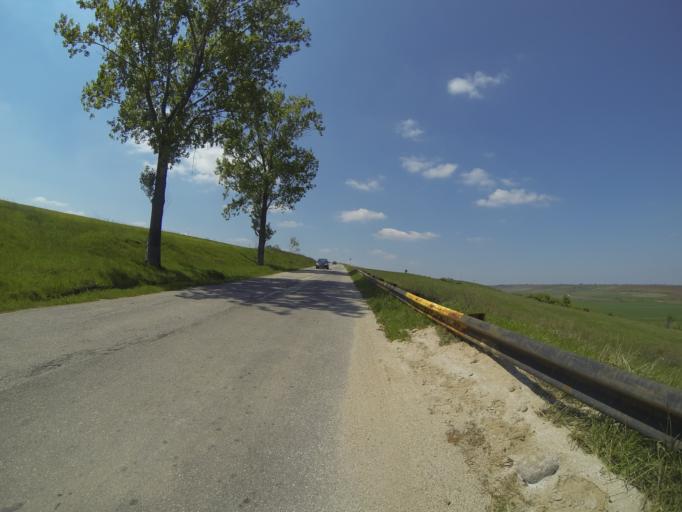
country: RO
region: Dolj
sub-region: Comuna Salcuta
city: Salcuta
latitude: 44.2571
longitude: 23.4421
